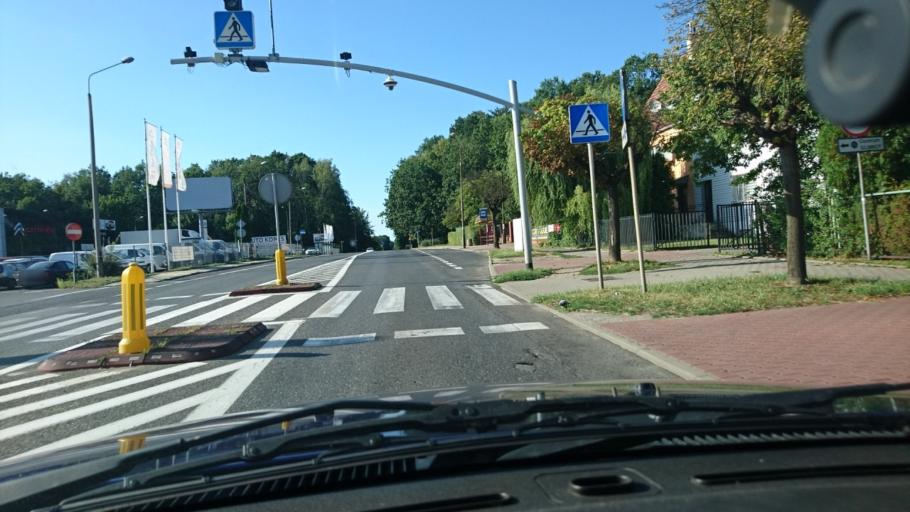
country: PL
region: Silesian Voivodeship
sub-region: Gliwice
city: Gliwice
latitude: 50.3246
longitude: 18.6617
